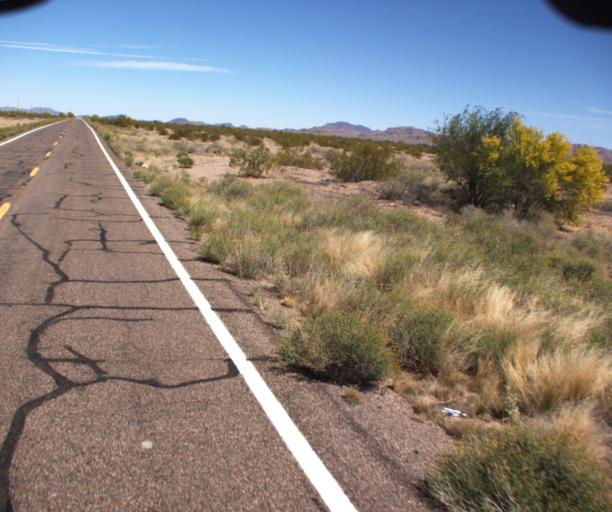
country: US
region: Arizona
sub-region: Pima County
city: Ajo
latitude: 32.6195
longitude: -112.8669
